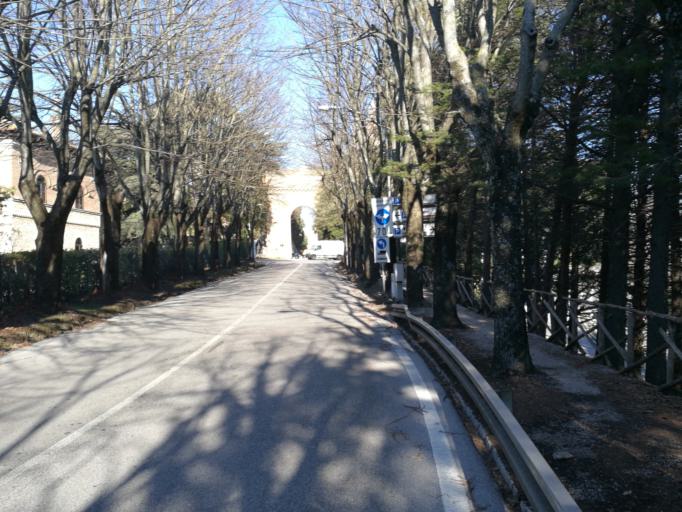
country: IT
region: Umbria
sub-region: Provincia di Perugia
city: Perugia
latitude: 43.0991
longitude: 12.3963
